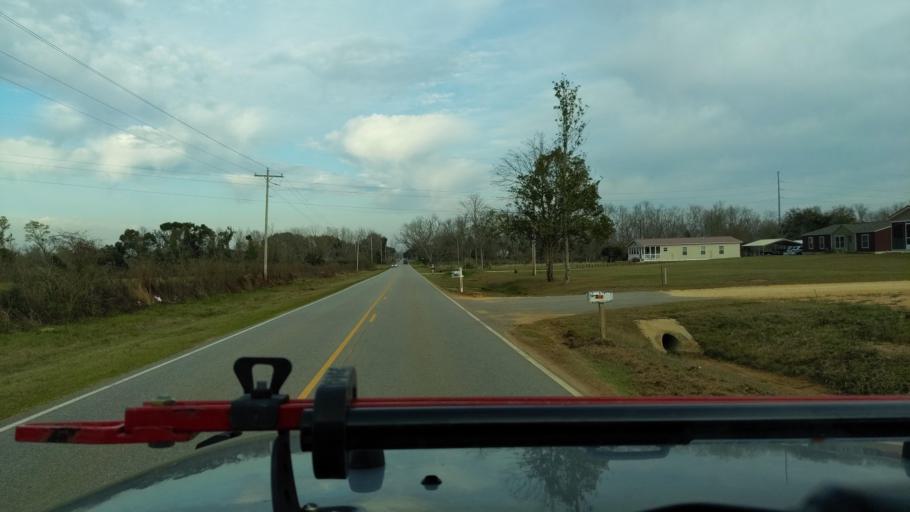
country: US
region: Alabama
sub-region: Baldwin County
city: Foley
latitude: 30.4579
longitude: -87.7535
